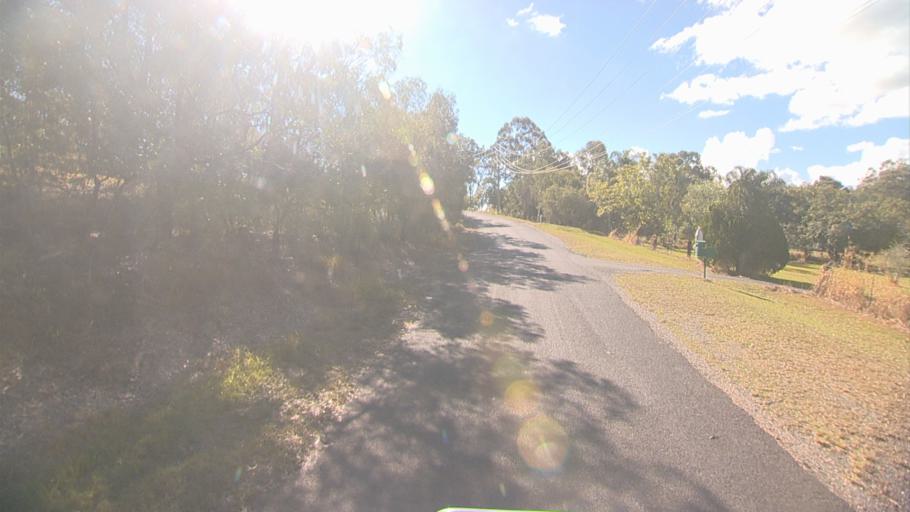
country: AU
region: Queensland
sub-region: Logan
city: Chambers Flat
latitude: -27.8119
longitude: 153.0893
